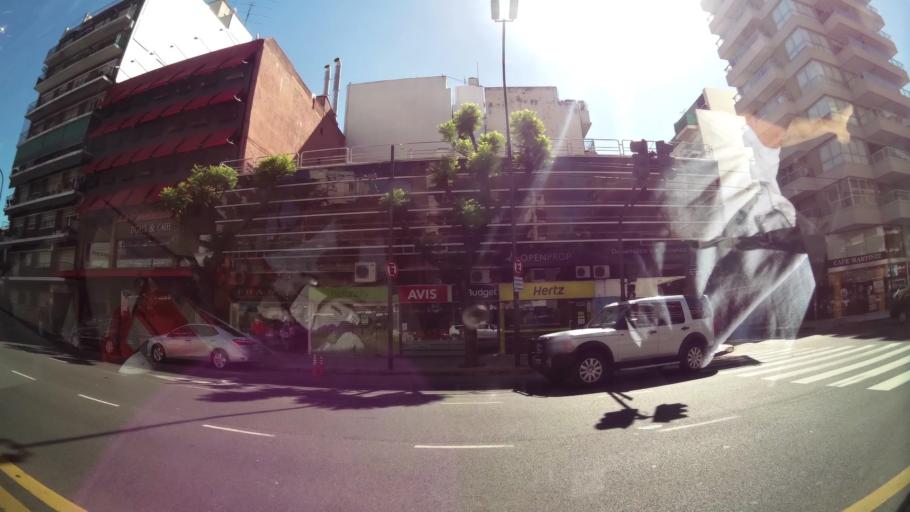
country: AR
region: Buenos Aires F.D.
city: Colegiales
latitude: -34.5585
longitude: -58.4461
